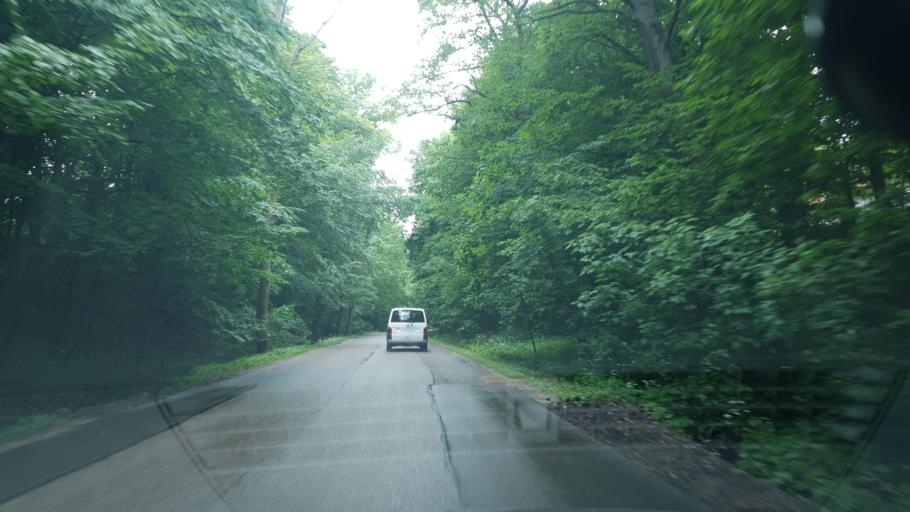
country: PL
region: Pomeranian Voivodeship
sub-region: Powiat kartuski
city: Przodkowo
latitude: 54.3588
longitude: 18.2519
